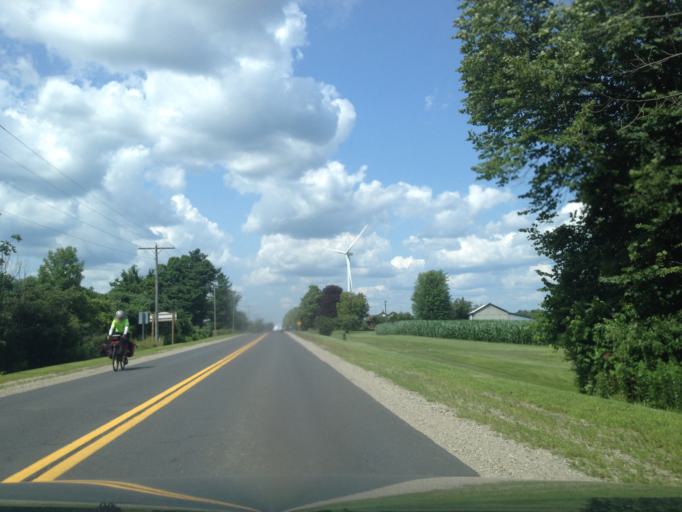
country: CA
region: Ontario
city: Aylmer
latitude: 42.6556
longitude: -80.8101
